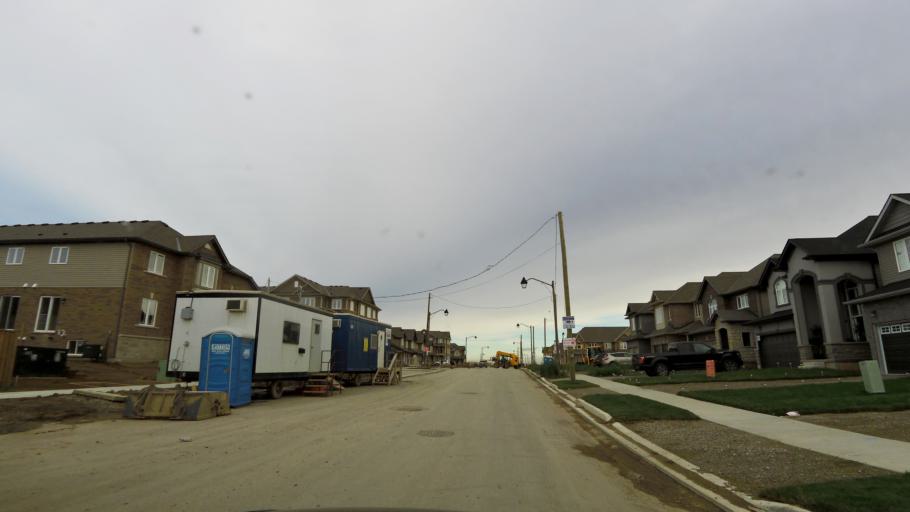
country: CA
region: Ontario
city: Hamilton
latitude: 43.1765
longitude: -79.7994
